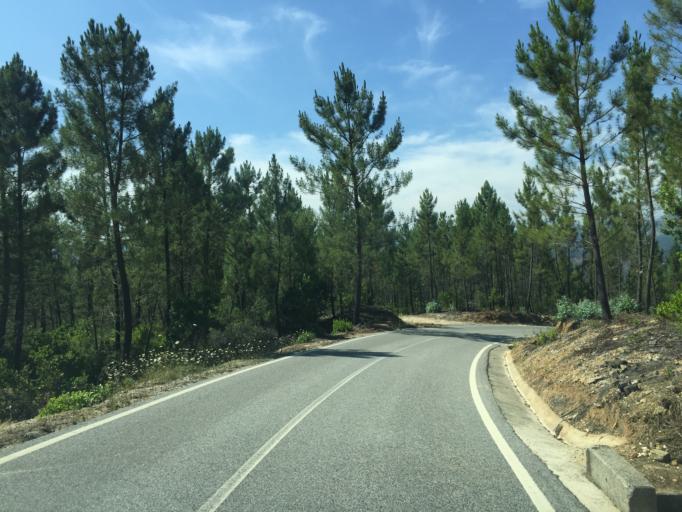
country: PT
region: Castelo Branco
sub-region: Oleiros
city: Oleiros
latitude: 40.0007
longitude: -7.8444
